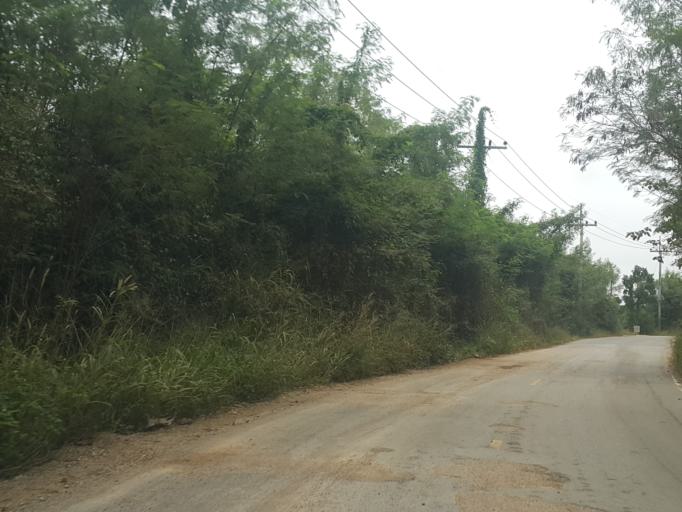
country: TH
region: Lampang
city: Lampang
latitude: 18.3345
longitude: 99.4857
